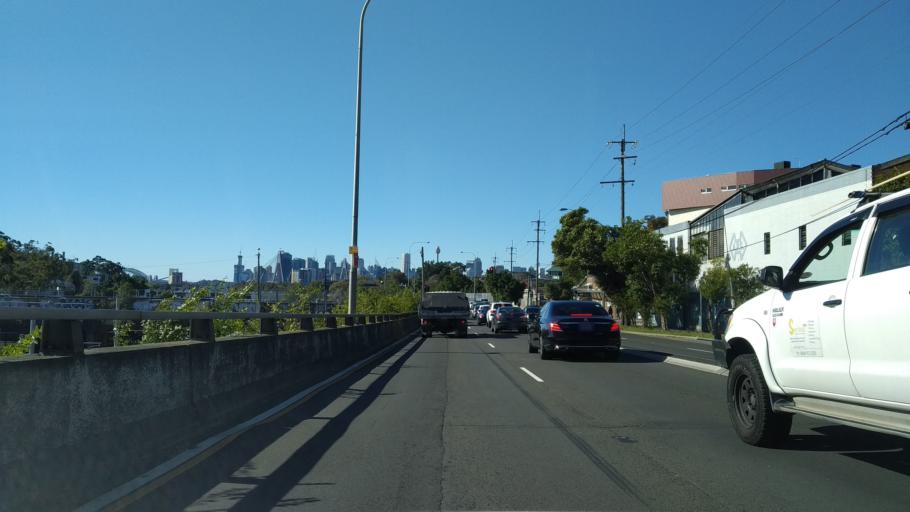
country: AU
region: New South Wales
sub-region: Leichhardt
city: Lilyfield
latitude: -33.8744
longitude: 151.1632
